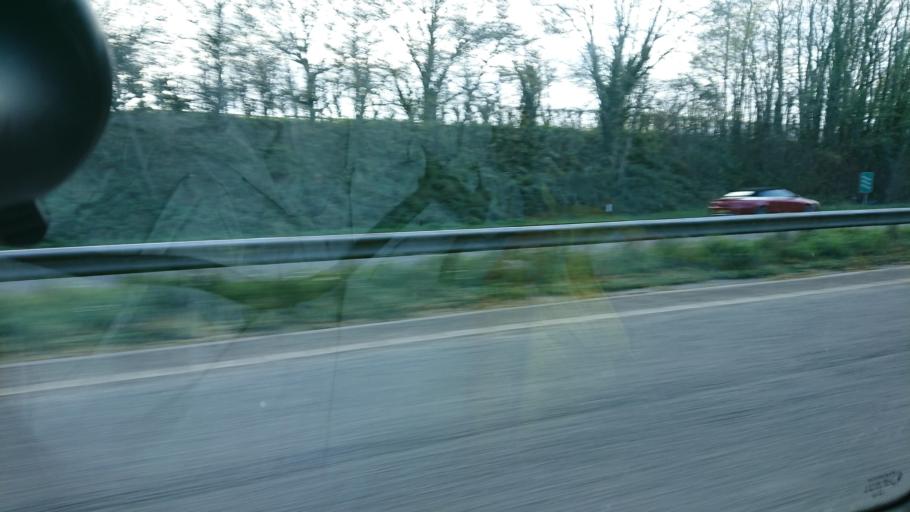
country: GB
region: England
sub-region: Devon
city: Yealmpton
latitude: 50.3798
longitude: -4.0132
